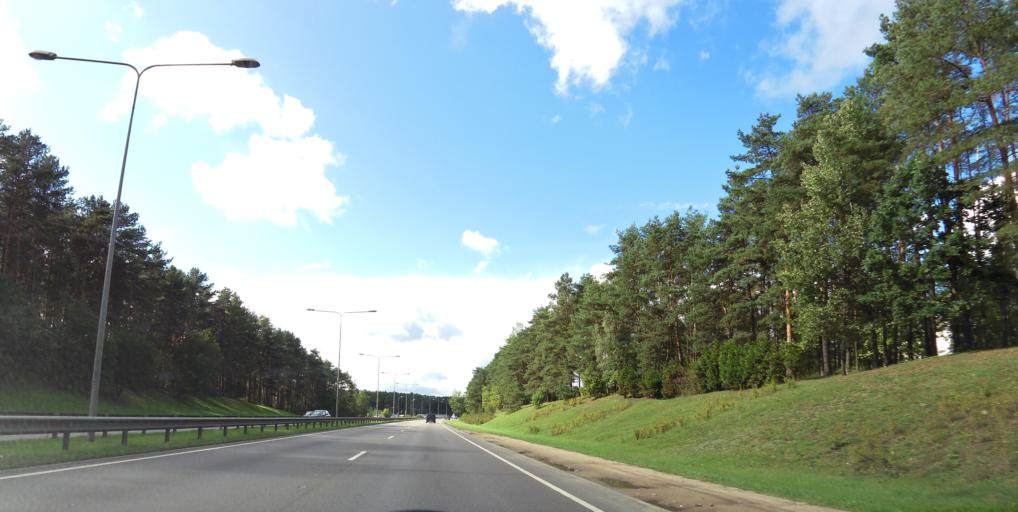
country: LT
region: Vilnius County
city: Lazdynai
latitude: 54.6706
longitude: 25.2136
